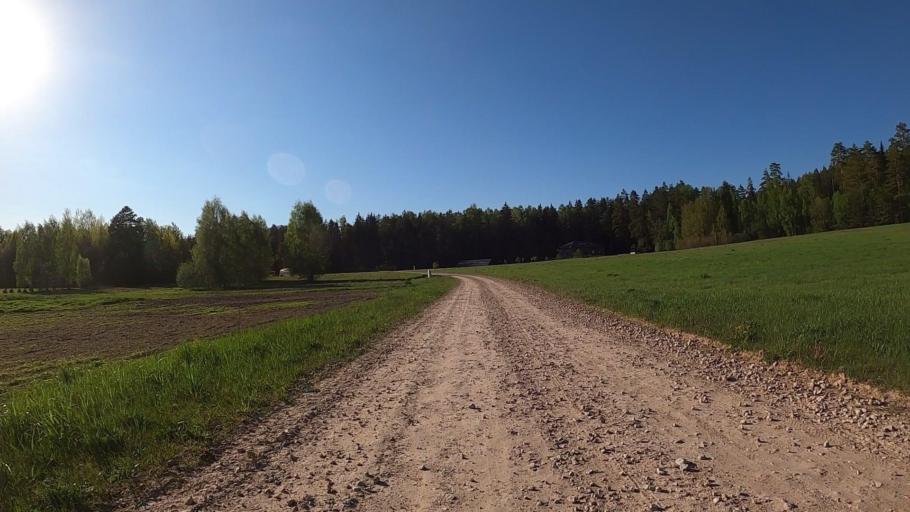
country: LV
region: Baldone
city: Baldone
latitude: 56.7643
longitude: 24.3727
